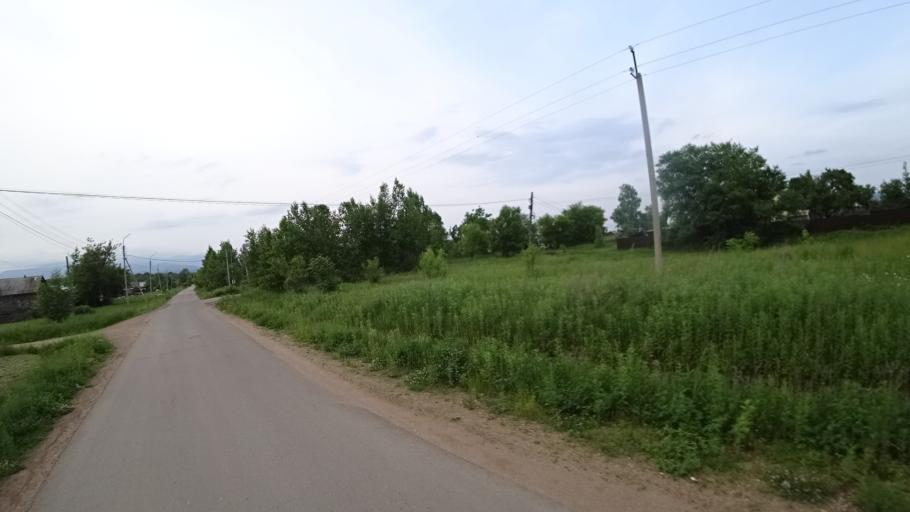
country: RU
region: Primorskiy
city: Novosysoyevka
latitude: 44.2350
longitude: 133.3592
